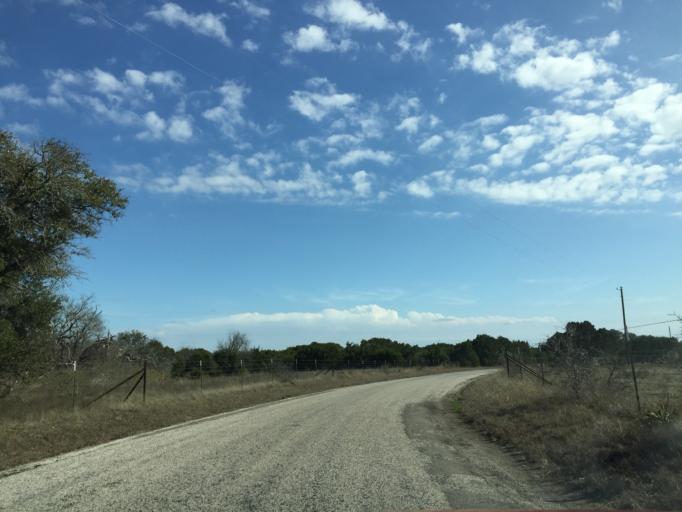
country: US
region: Texas
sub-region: Williamson County
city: Florence
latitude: 30.7800
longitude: -97.8913
